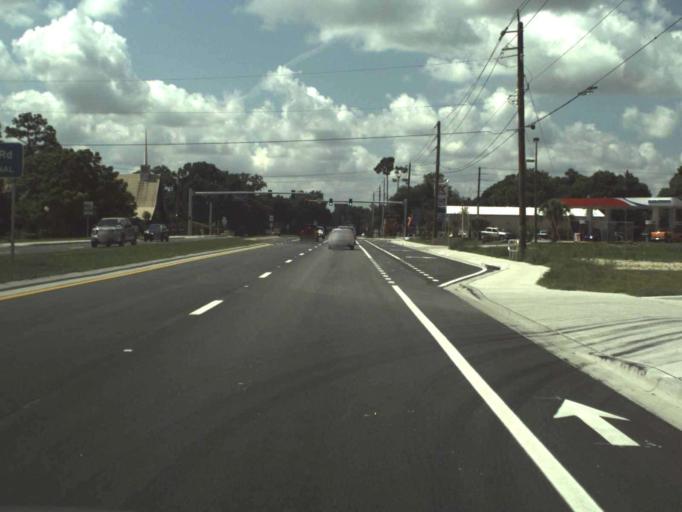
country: US
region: Florida
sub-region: Seminole County
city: Midway
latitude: 28.8517
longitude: -81.1622
